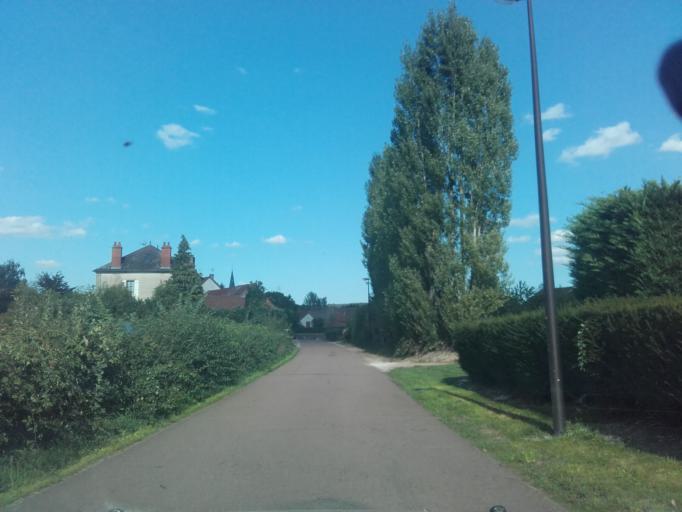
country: FR
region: Bourgogne
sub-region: Departement de Saone-et-Loire
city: Epinac
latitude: 47.0061
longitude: 4.4693
